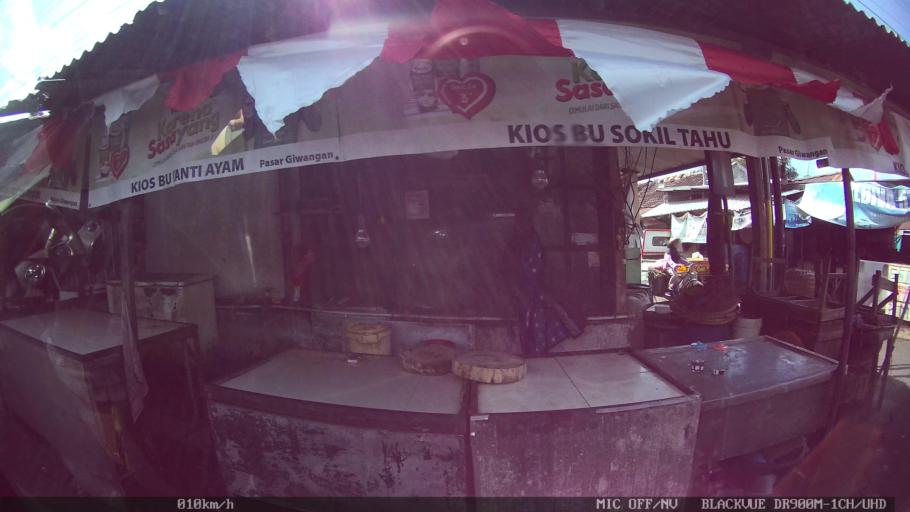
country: ID
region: Daerah Istimewa Yogyakarta
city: Sewon
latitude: -7.8318
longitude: 110.3883
